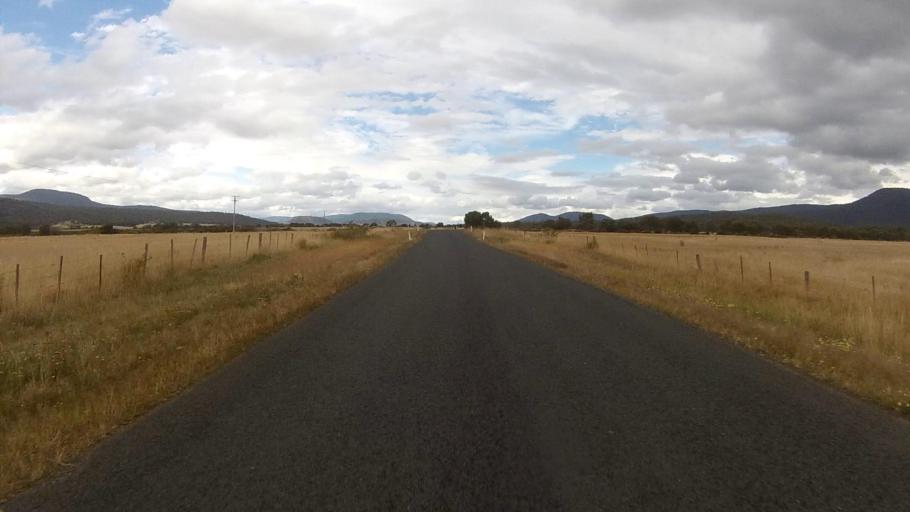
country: AU
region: Tasmania
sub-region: Break O'Day
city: St Helens
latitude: -41.8236
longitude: 147.8677
